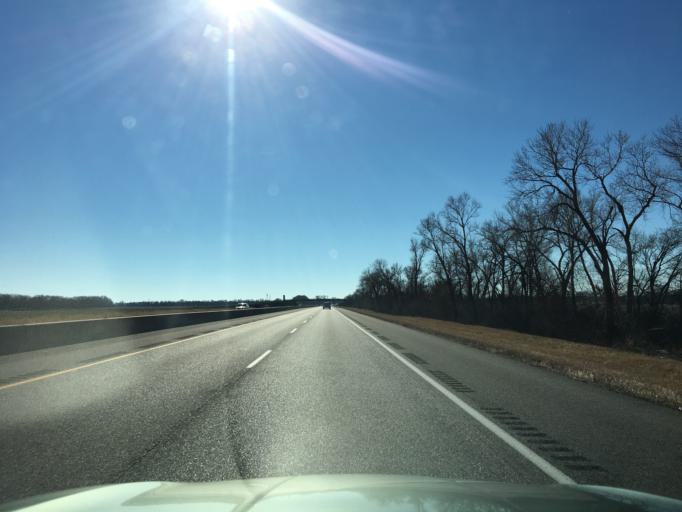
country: US
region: Kansas
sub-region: Sumner County
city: Belle Plaine
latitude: 37.4263
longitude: -97.3213
